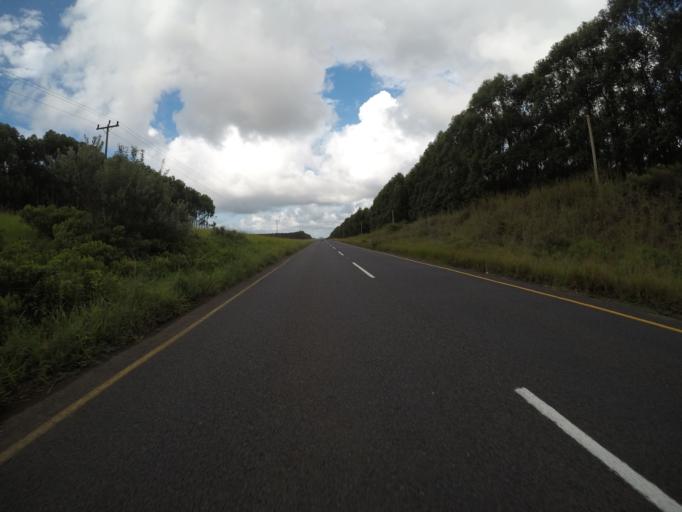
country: ZA
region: KwaZulu-Natal
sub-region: uMkhanyakude District Municipality
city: Mtubatuba
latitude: -28.3917
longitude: 32.2255
